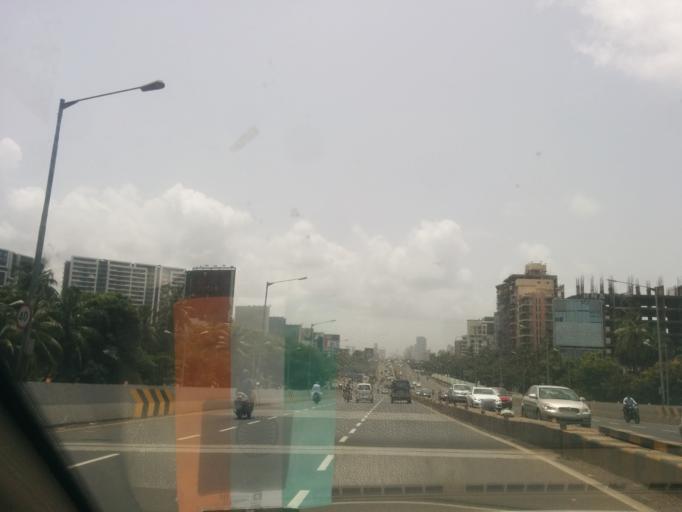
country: IN
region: Maharashtra
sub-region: Mumbai Suburban
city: Mumbai
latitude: 19.0607
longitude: 72.8465
